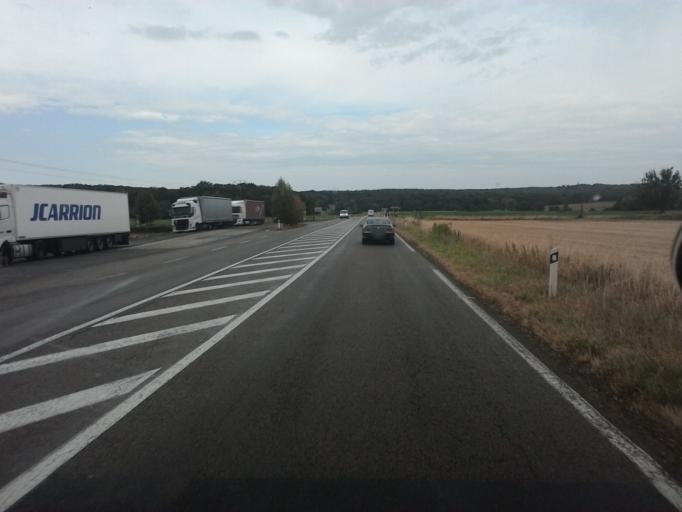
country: FR
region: Franche-Comte
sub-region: Departement du Jura
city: Poligny
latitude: 46.8453
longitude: 5.6422
